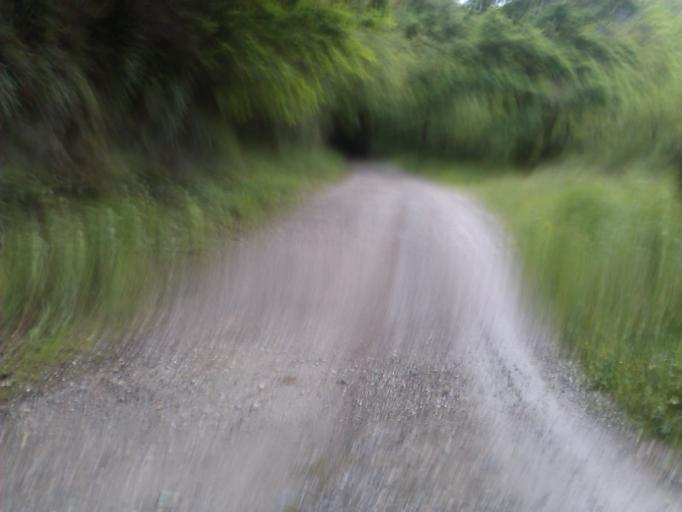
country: ES
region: Basque Country
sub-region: Provincia de Guipuzcoa
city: Elduayen
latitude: 43.1739
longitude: -1.9695
